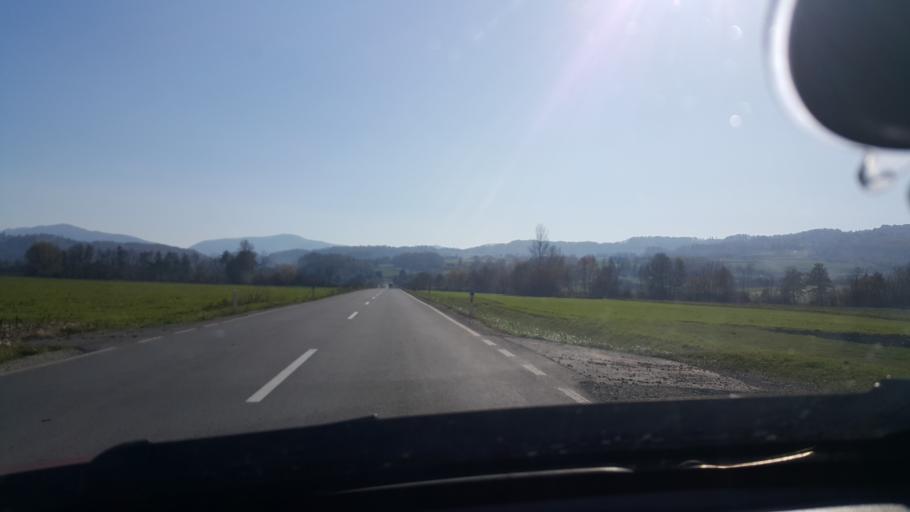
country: SI
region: Kozje
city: Kozje
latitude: 46.0971
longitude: 15.6131
